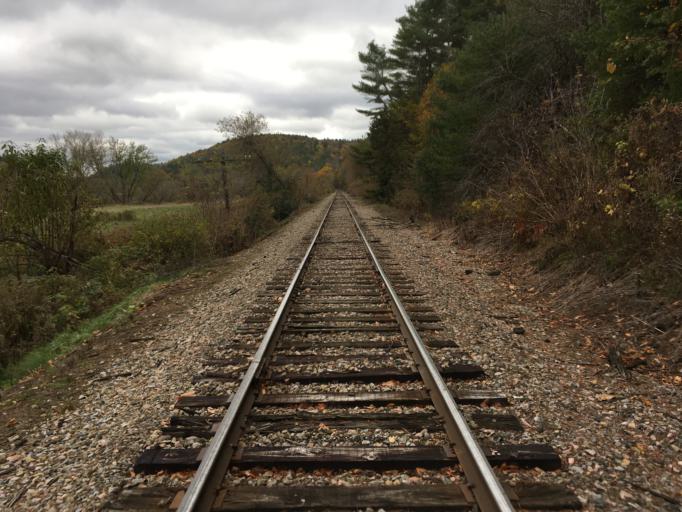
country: US
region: New Hampshire
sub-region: Grafton County
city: Woodsville
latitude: 44.1954
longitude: -72.0658
